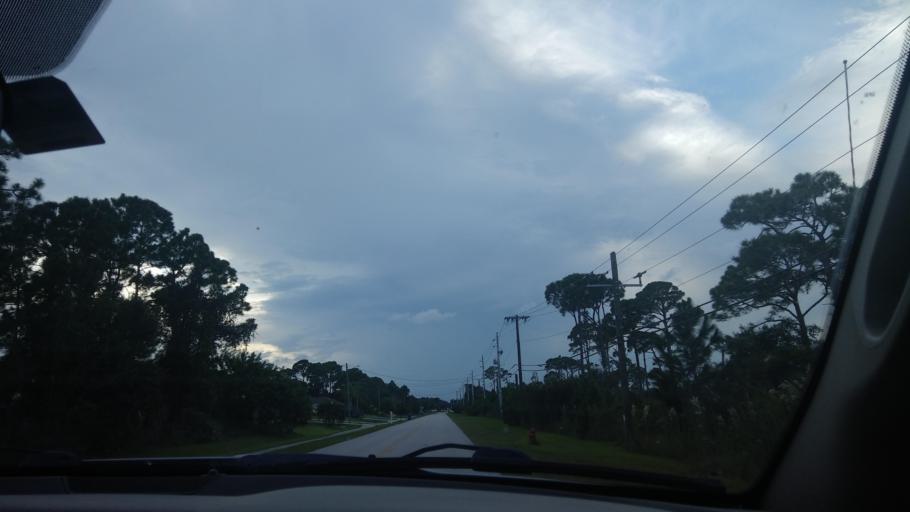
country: US
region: Florida
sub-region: Indian River County
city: Sebastian
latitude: 27.7778
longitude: -80.4702
